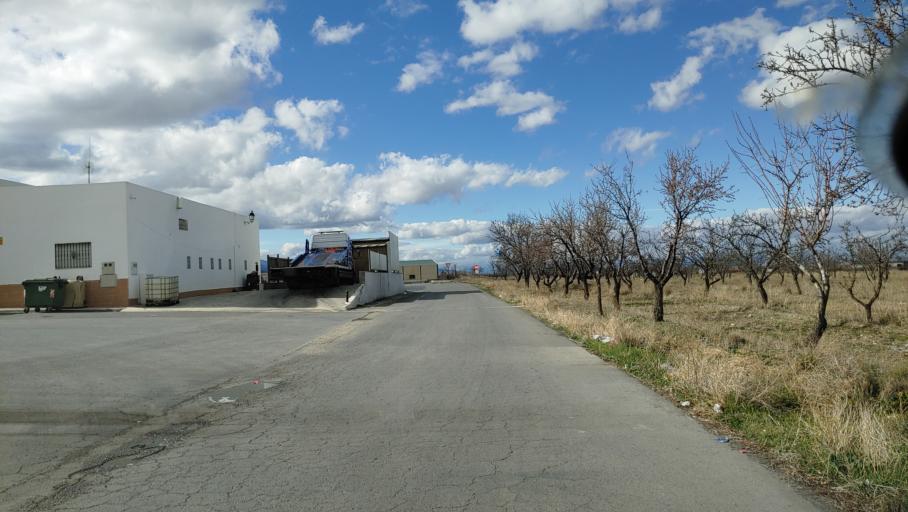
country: ES
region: Andalusia
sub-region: Provincia de Granada
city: Hueneja
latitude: 37.1958
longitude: -2.9842
